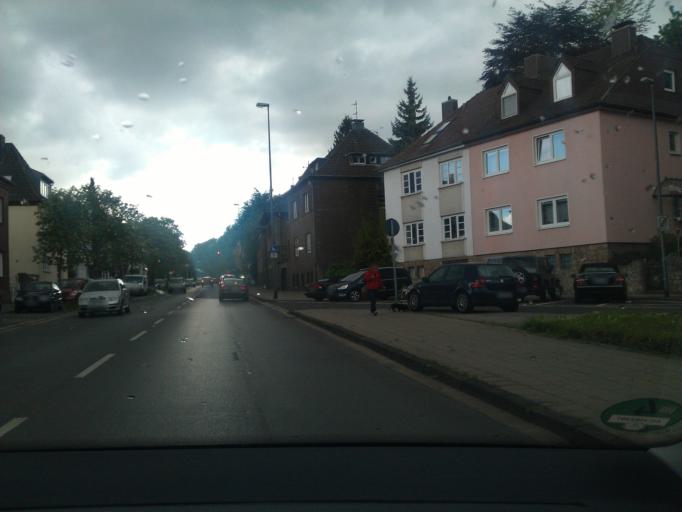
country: DE
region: North Rhine-Westphalia
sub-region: Regierungsbezirk Koln
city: Aachen
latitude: 50.7642
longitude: 6.0747
